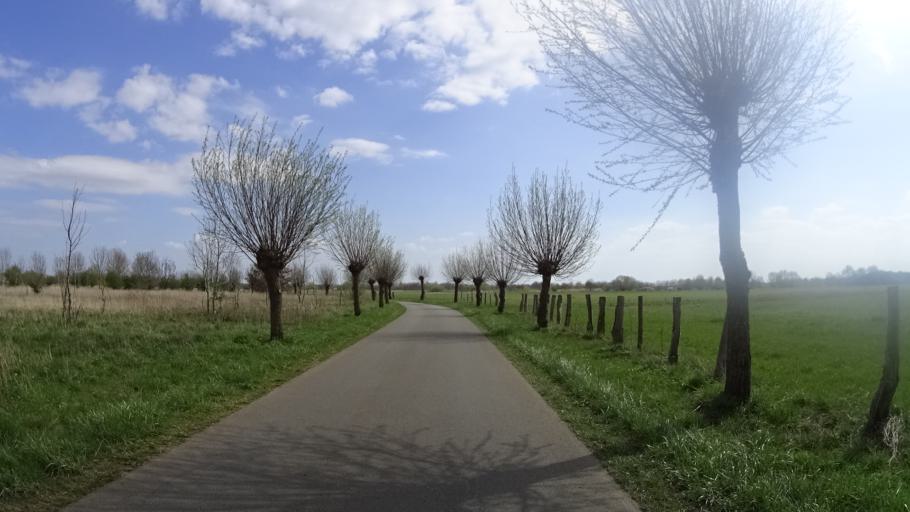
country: DE
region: Lower Saxony
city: Rhede
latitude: 53.0585
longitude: 7.2911
